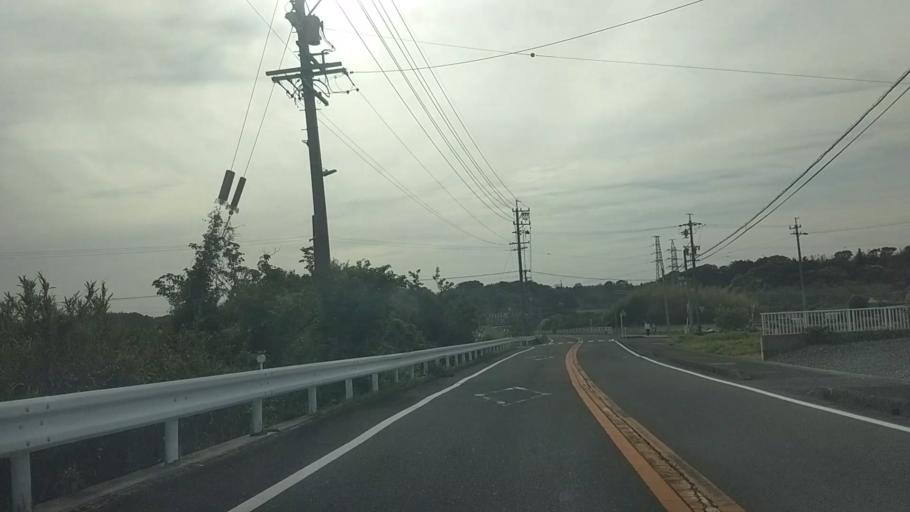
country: JP
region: Shizuoka
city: Kosai-shi
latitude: 34.7463
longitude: 137.6077
